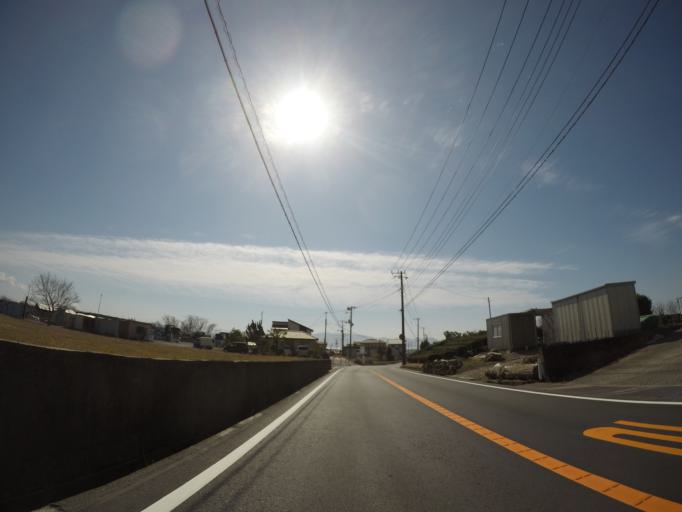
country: JP
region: Shizuoka
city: Numazu
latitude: 35.1329
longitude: 138.8362
